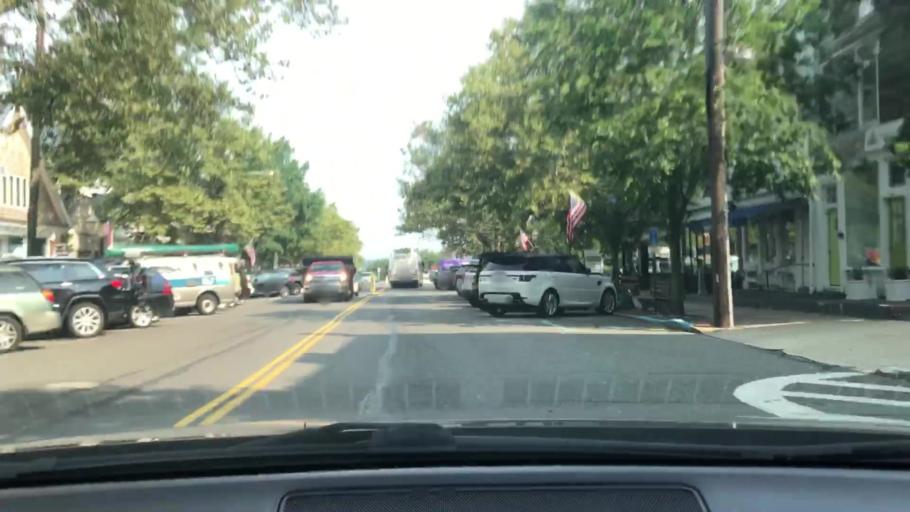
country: US
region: New York
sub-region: Suffolk County
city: Sag Harbor
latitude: 41.0011
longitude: -72.2953
